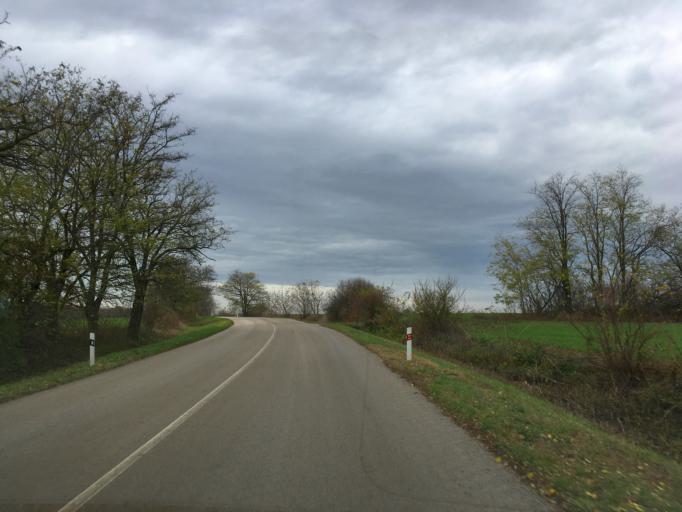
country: SK
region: Nitriansky
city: Svodin
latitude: 48.0286
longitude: 18.3987
